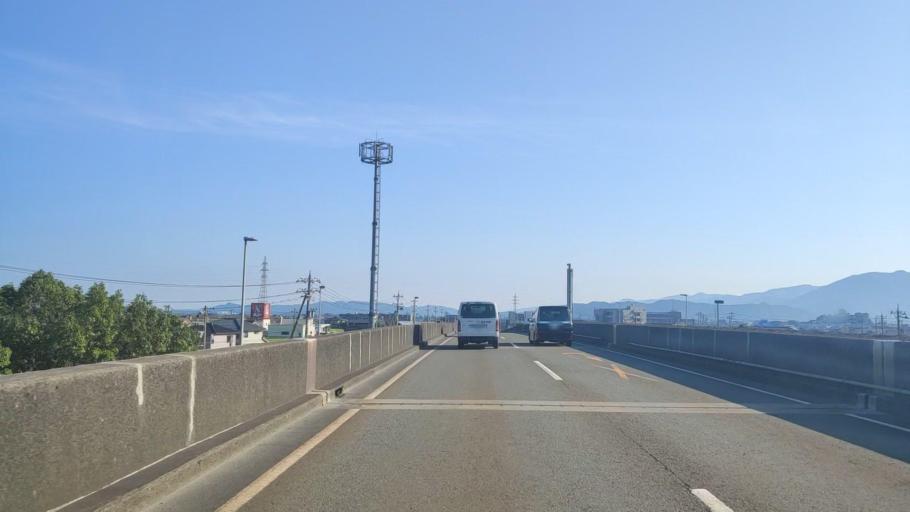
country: JP
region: Fukui
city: Maruoka
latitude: 36.1429
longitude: 136.2640
